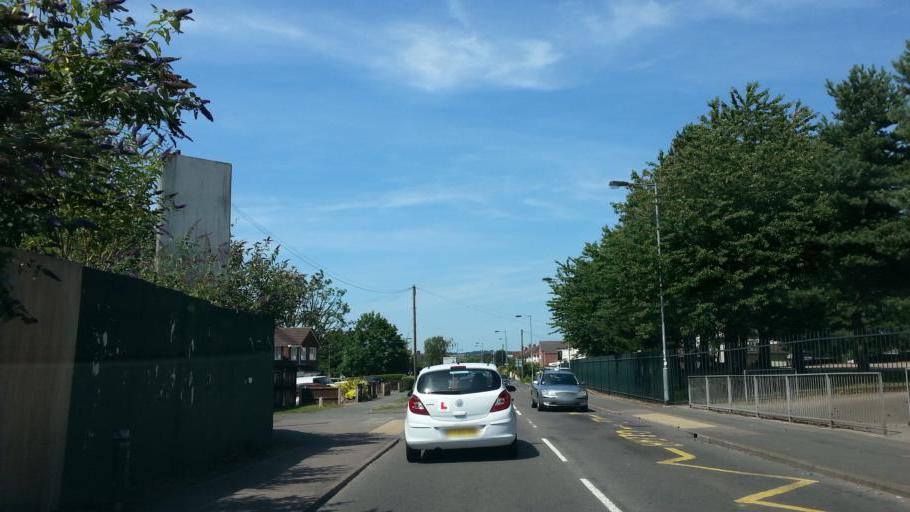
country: GB
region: England
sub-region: Staffordshire
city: Norton Canes
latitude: 52.6929
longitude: -1.9879
